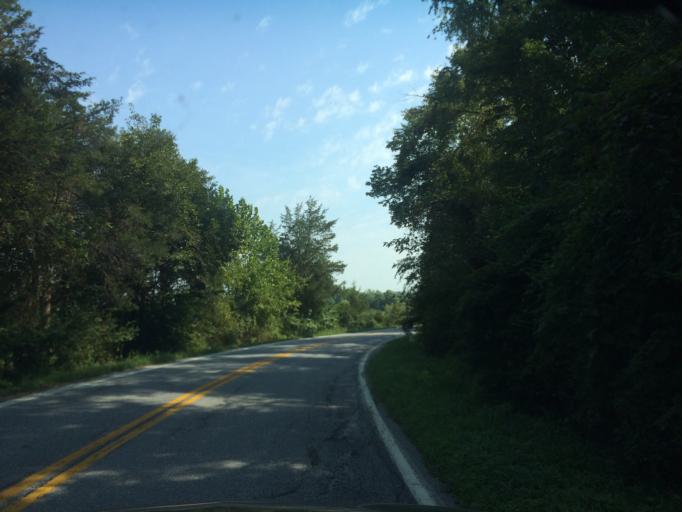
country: US
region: Maryland
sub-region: Carroll County
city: New Windsor
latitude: 39.6067
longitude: -77.1159
